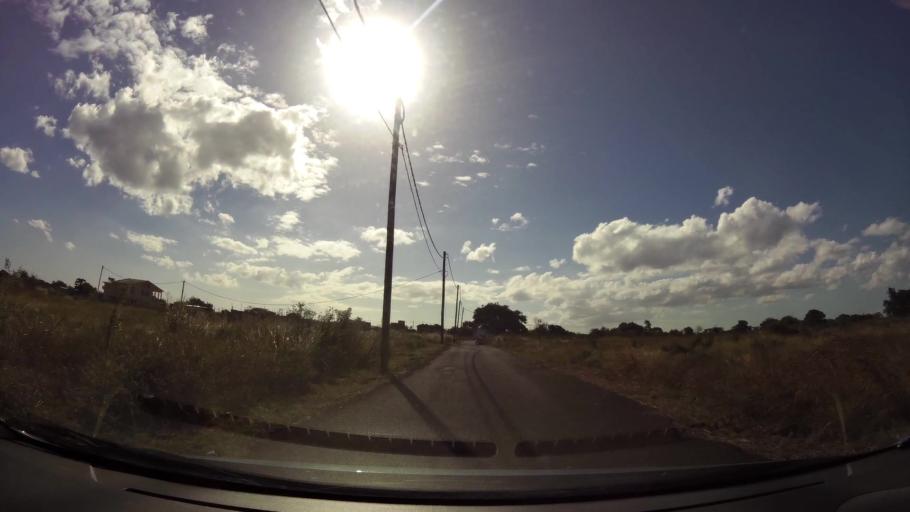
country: MU
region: Black River
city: Gros Cailloux
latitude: -20.2028
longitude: 57.4156
